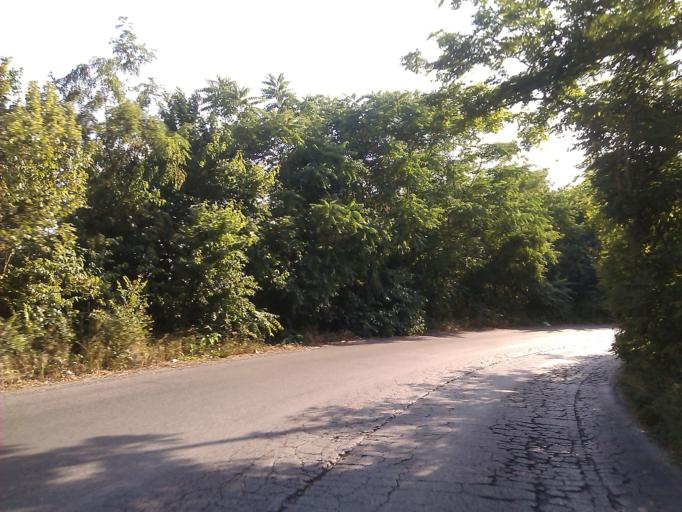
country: IT
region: Latium
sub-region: Citta metropolitana di Roma Capitale
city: Borgo Lotti
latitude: 41.8274
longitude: 12.5339
